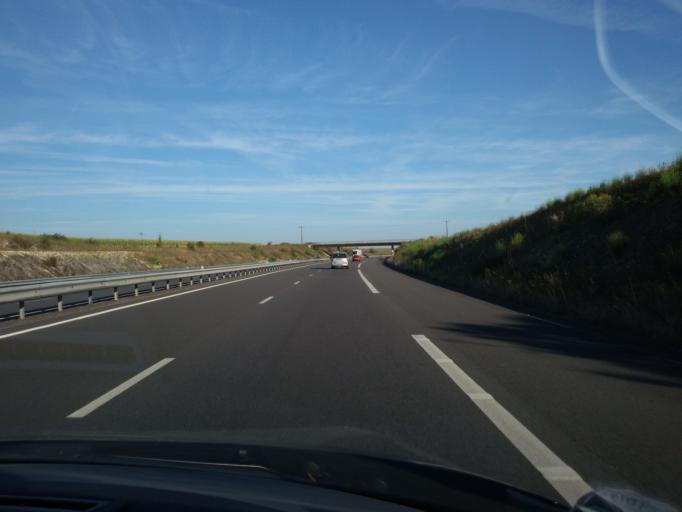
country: FR
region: Centre
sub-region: Departement du Cher
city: Trouy
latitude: 47.0087
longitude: 2.3894
